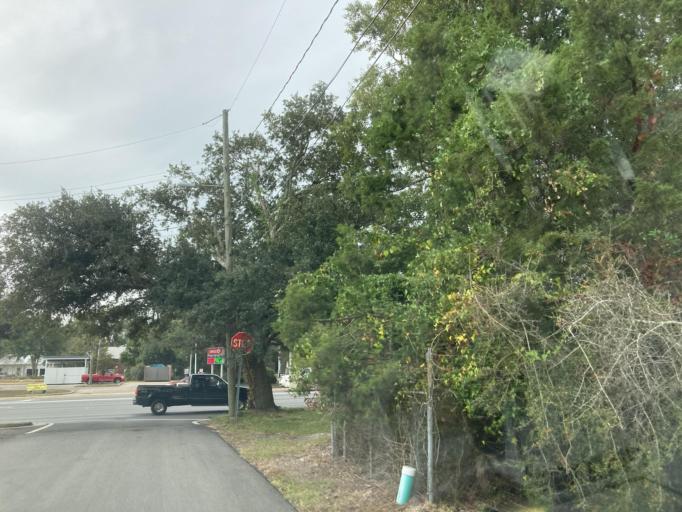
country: US
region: Mississippi
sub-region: Jackson County
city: Ocean Springs
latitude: 30.4165
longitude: -88.8264
